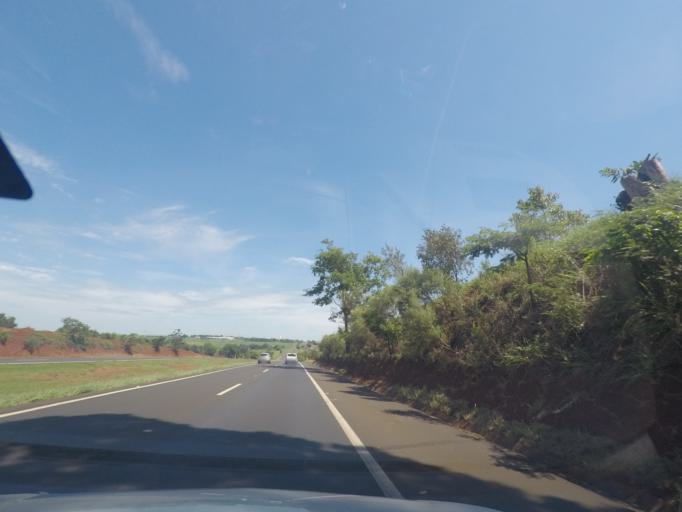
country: BR
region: Sao Paulo
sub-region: Araraquara
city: Araraquara
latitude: -21.8026
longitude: -48.2003
